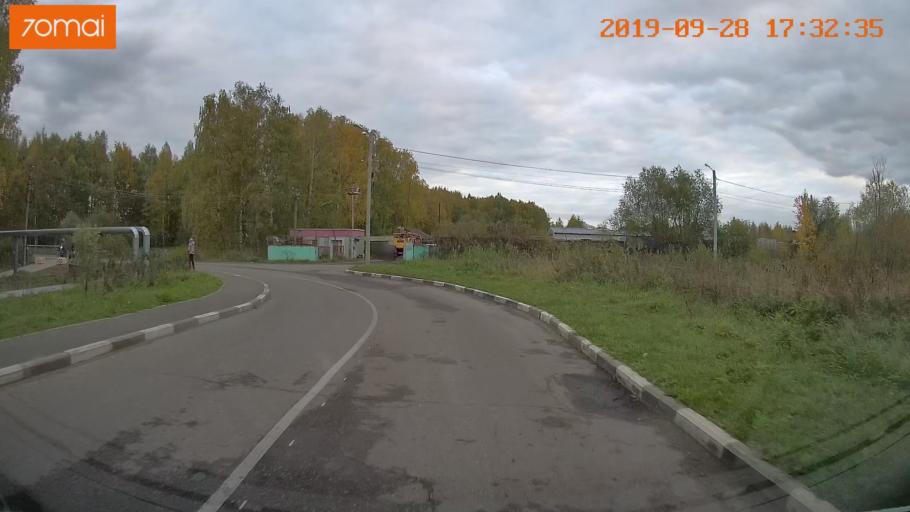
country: RU
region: Jaroslavl
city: Yaroslavl
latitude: 57.5699
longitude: 39.9187
